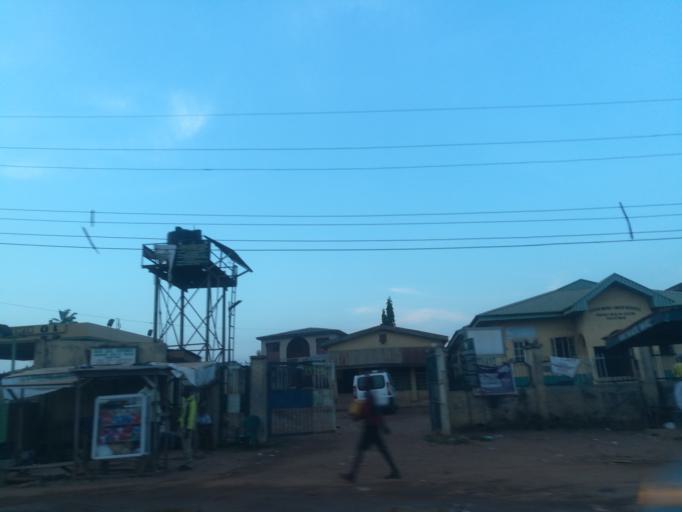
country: NG
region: Ogun
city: Abeokuta
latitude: 7.1784
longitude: 3.3957
